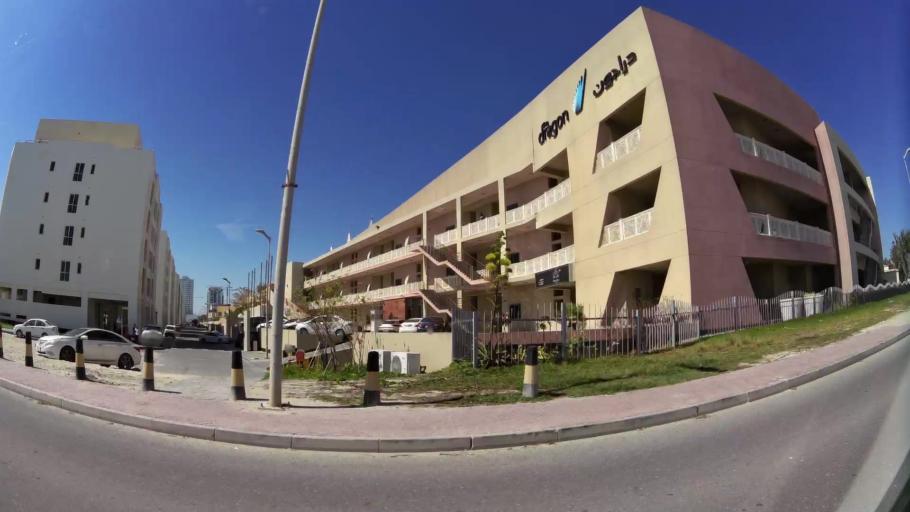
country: BH
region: Muharraq
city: Al Hadd
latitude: 26.2862
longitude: 50.6724
